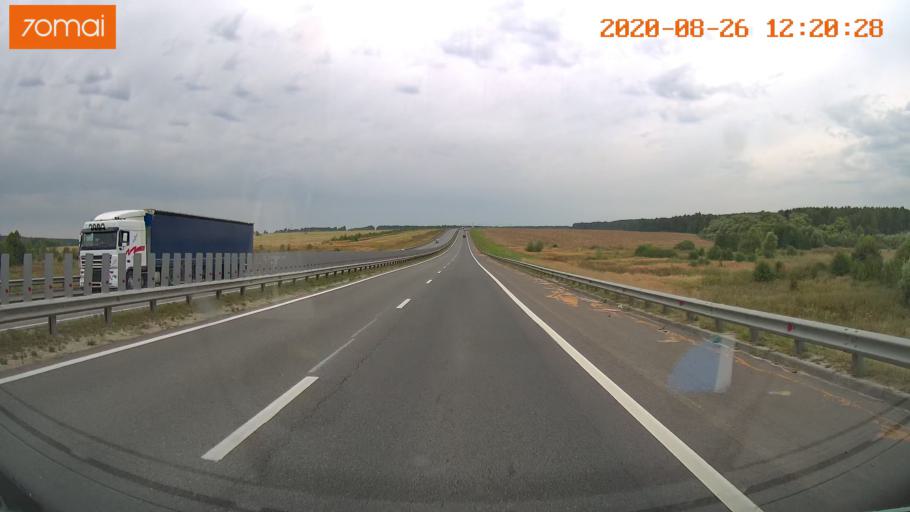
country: RU
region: Rjazan
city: Murmino
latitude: 54.4869
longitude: 39.9680
